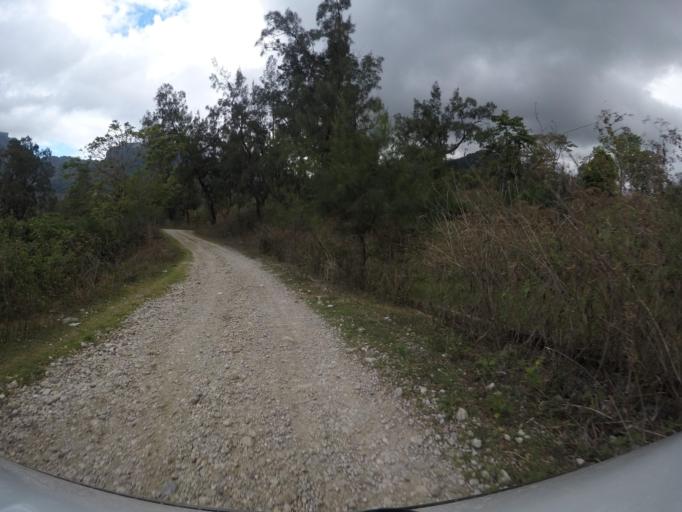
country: TL
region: Baucau
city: Venilale
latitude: -8.6717
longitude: 126.6333
